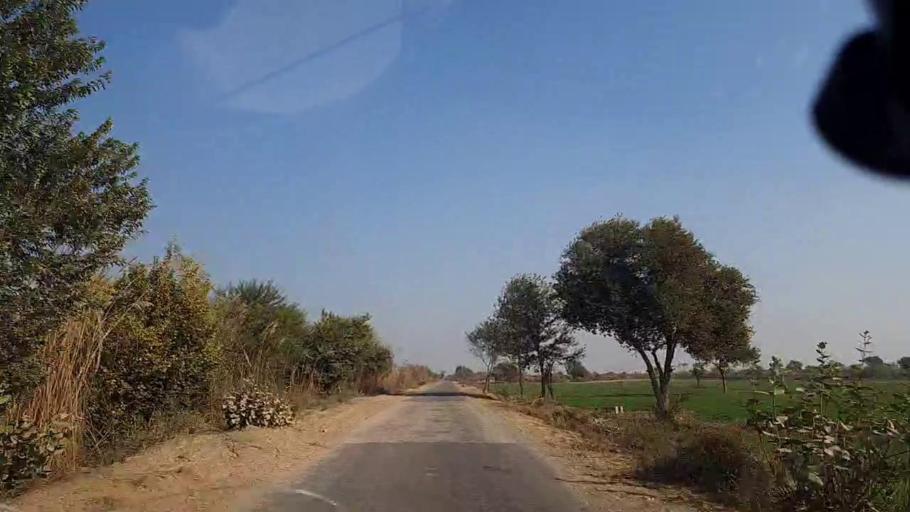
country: PK
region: Sindh
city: Khanpur
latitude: 27.6861
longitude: 69.5214
